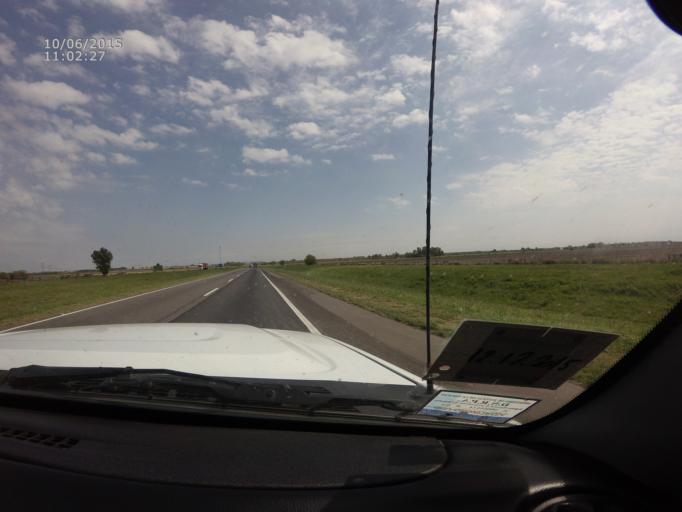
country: AR
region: Santa Fe
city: Villa Constitucion
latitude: -33.2478
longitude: -60.4315
